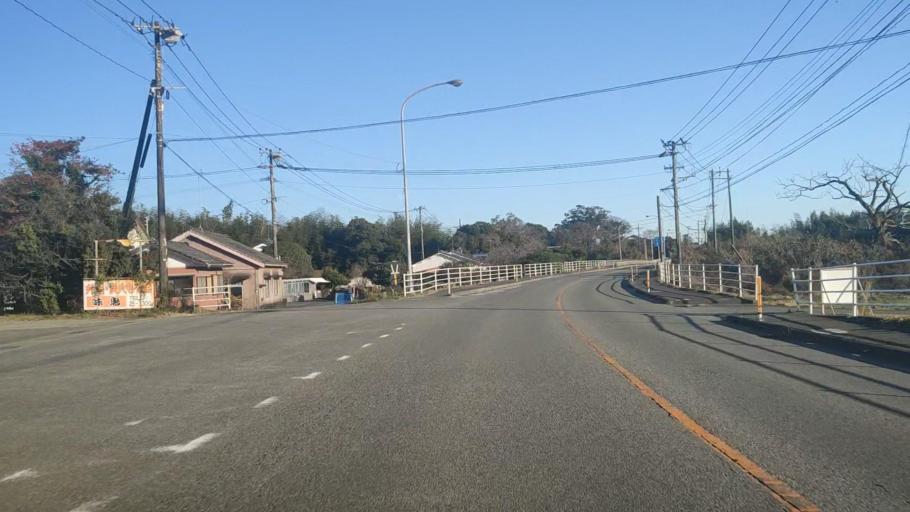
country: JP
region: Miyazaki
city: Takanabe
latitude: 32.2395
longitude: 131.5483
